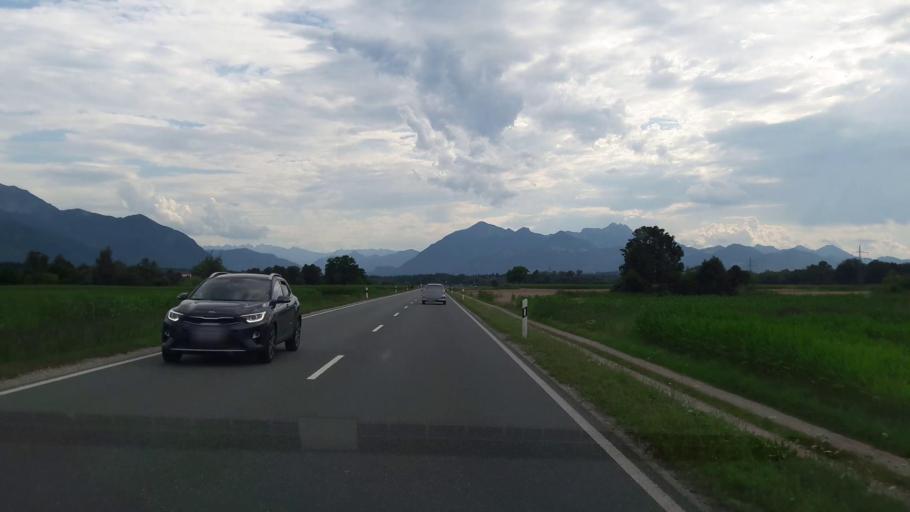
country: DE
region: Bavaria
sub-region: Upper Bavaria
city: Grabenstatt
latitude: 47.8413
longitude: 12.5333
